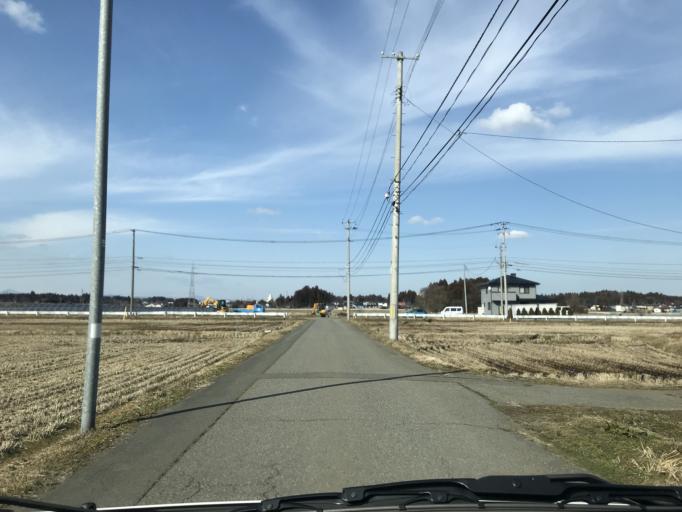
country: JP
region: Iwate
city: Kitakami
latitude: 39.3001
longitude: 141.0930
